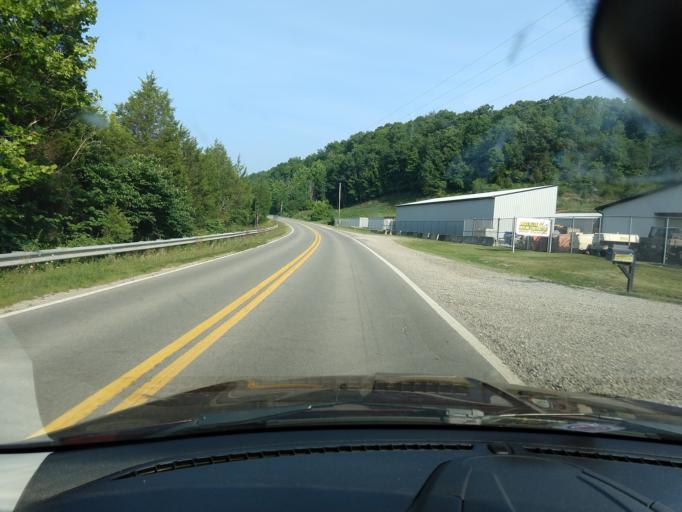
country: US
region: West Virginia
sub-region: Jackson County
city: Ripley
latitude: 38.8393
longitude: -81.7826
